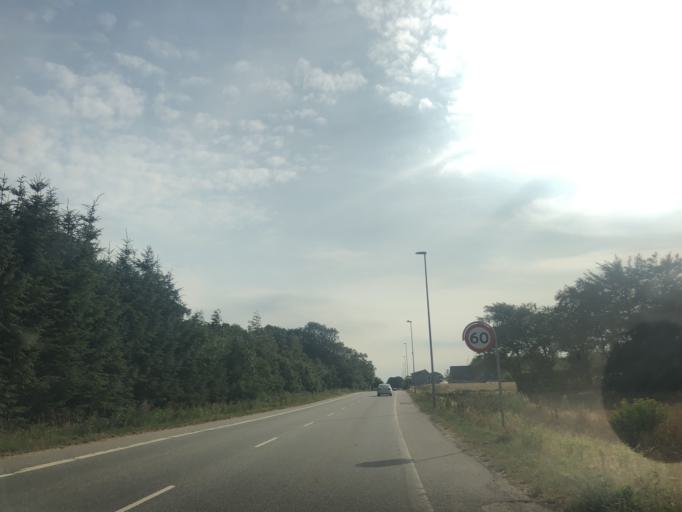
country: DK
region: Central Jutland
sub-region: Skive Kommune
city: Skive
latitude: 56.6468
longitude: 8.9303
